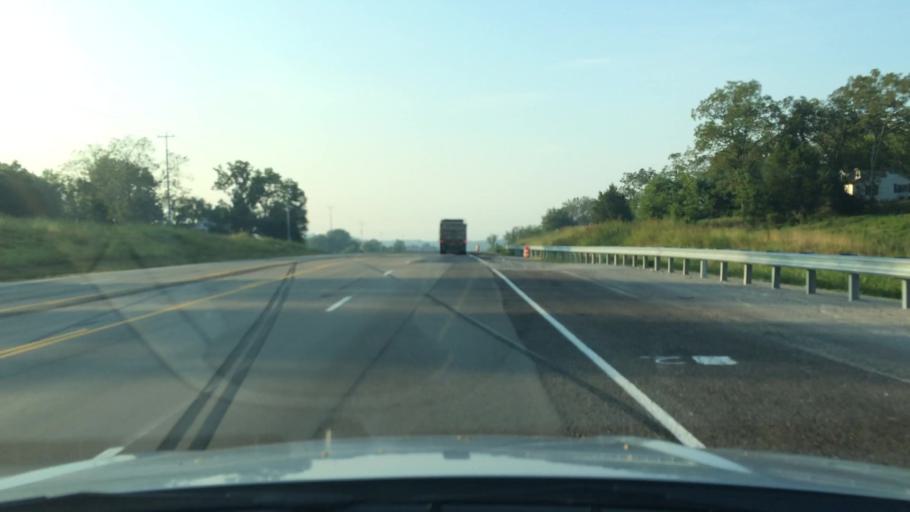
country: US
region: Tennessee
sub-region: Giles County
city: Pulaski
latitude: 35.1647
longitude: -87.0122
